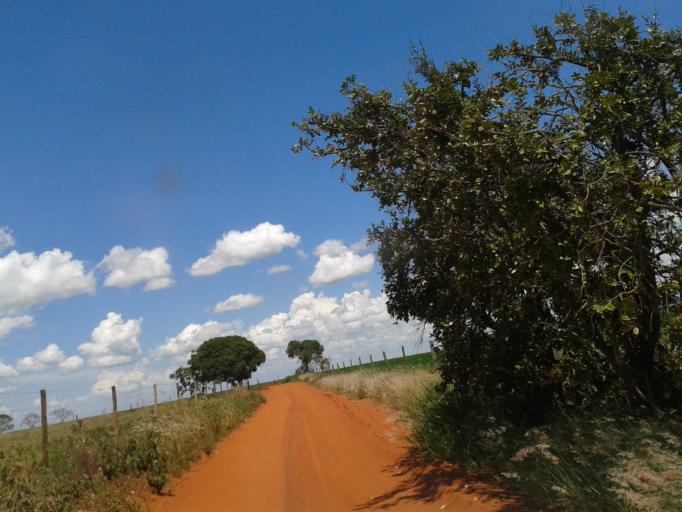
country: BR
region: Minas Gerais
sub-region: Centralina
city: Centralina
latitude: -18.6988
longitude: -49.1475
